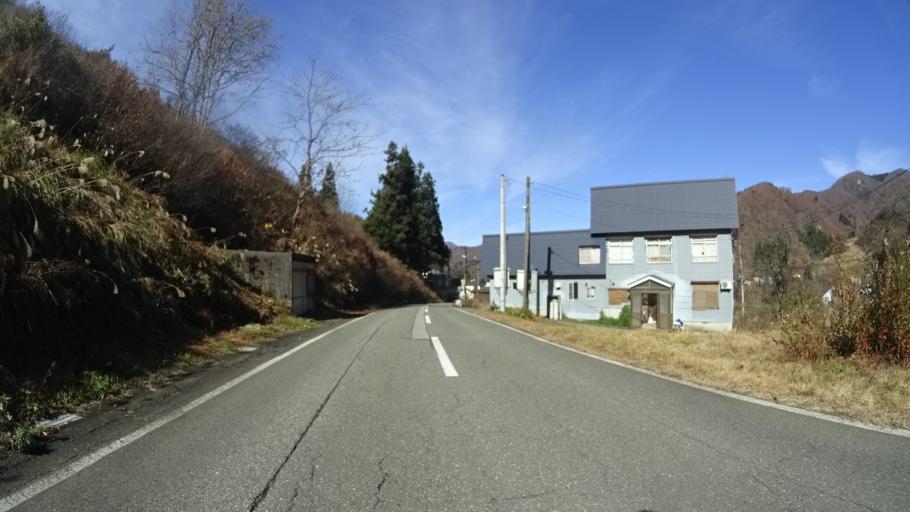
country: JP
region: Niigata
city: Muikamachi
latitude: 37.1903
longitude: 139.0812
